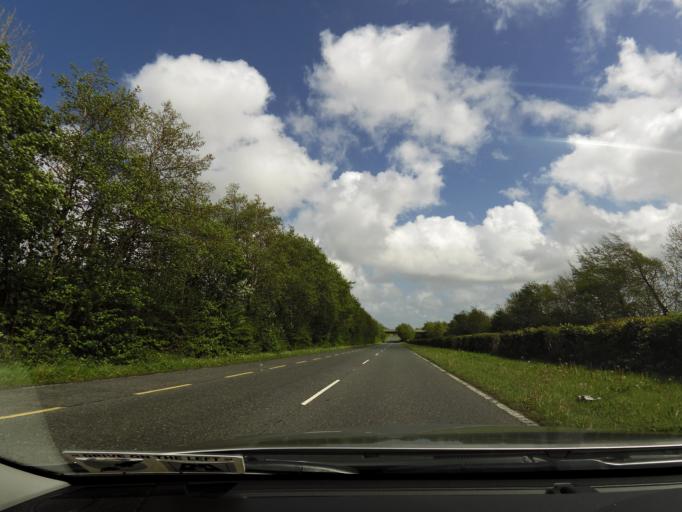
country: IE
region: Connaught
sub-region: County Galway
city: Oranmore
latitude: 53.2785
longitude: -8.9492
